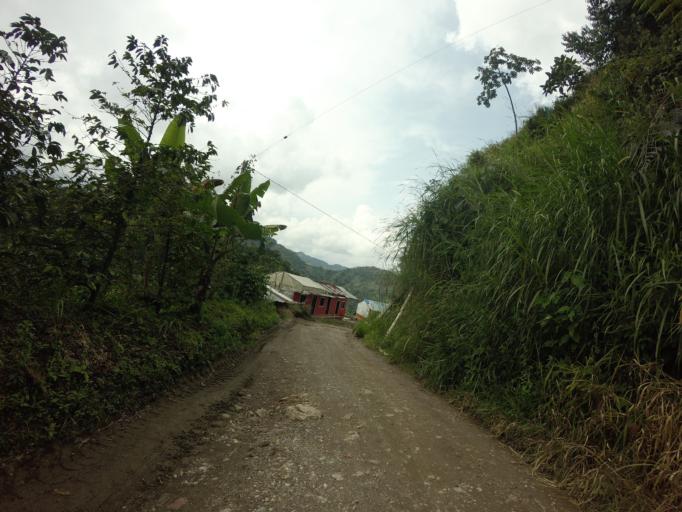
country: CO
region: Caldas
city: Marquetalia
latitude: 5.3133
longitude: -75.0505
